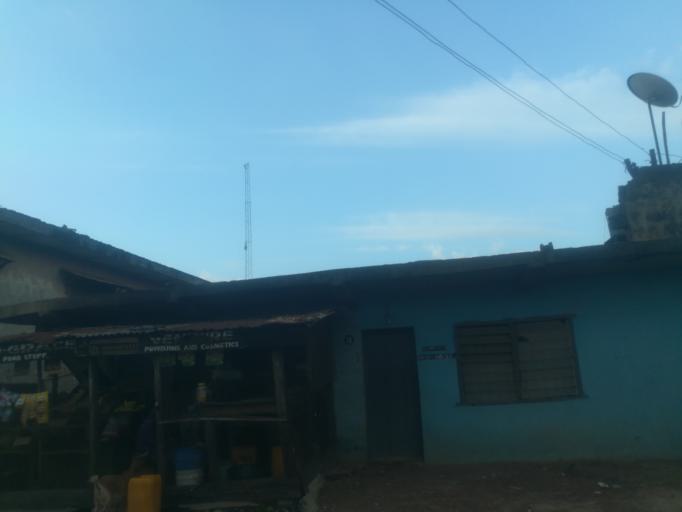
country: NG
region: Oyo
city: Ibadan
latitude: 7.4079
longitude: 3.9480
